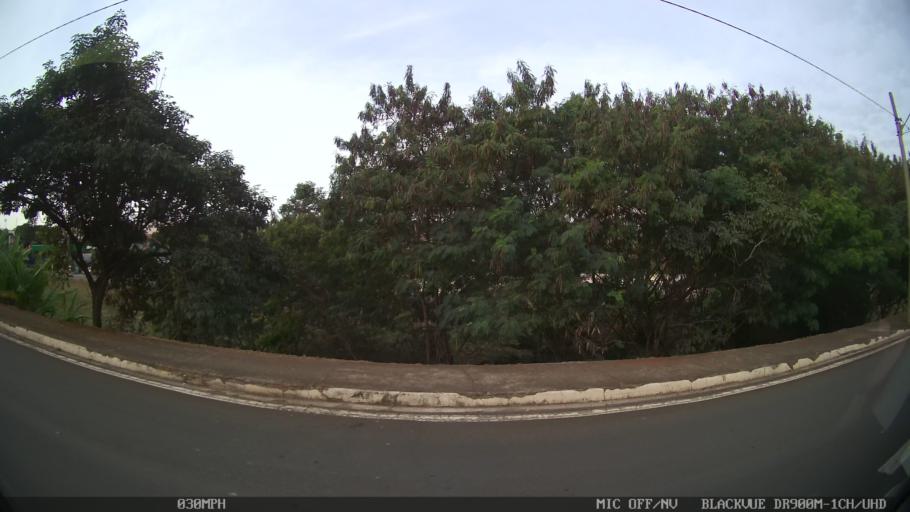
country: BR
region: Sao Paulo
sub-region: Limeira
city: Limeira
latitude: -22.5795
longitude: -47.4129
